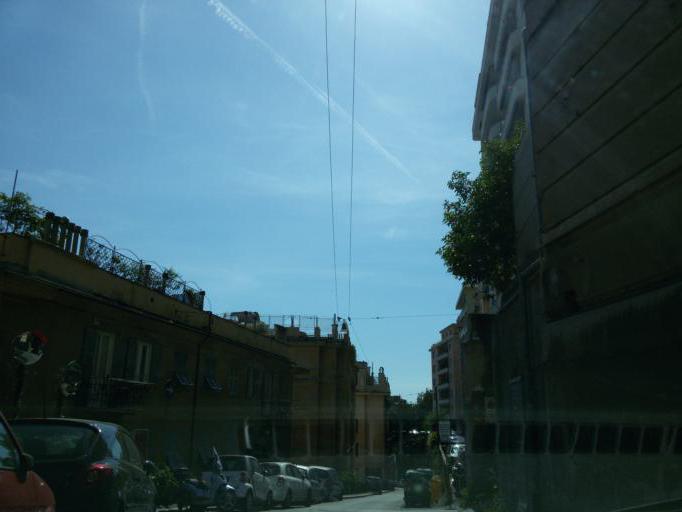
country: IT
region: Liguria
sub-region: Provincia di Genova
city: Genoa
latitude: 44.4180
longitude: 8.9369
